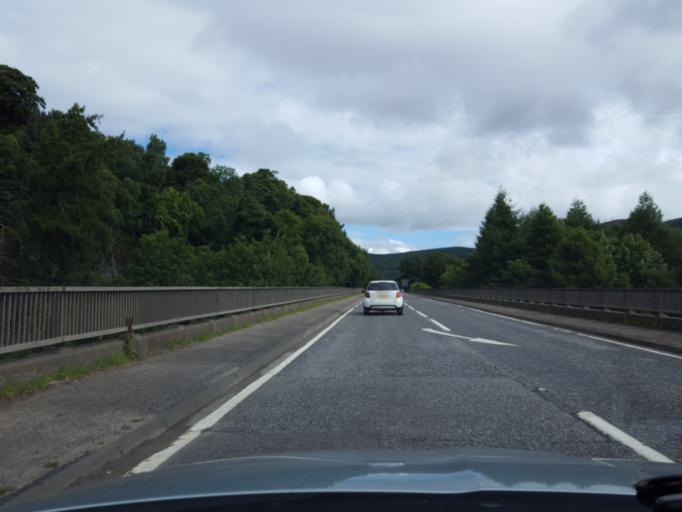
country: GB
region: Scotland
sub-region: Moray
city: Rothes
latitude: 57.4908
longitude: -3.1920
